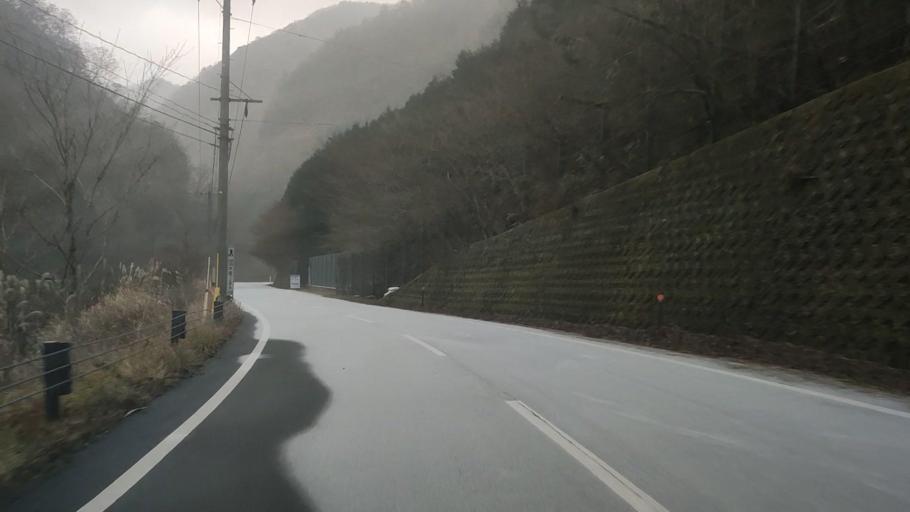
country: JP
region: Kumamoto
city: Matsubase
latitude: 32.5573
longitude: 130.9201
